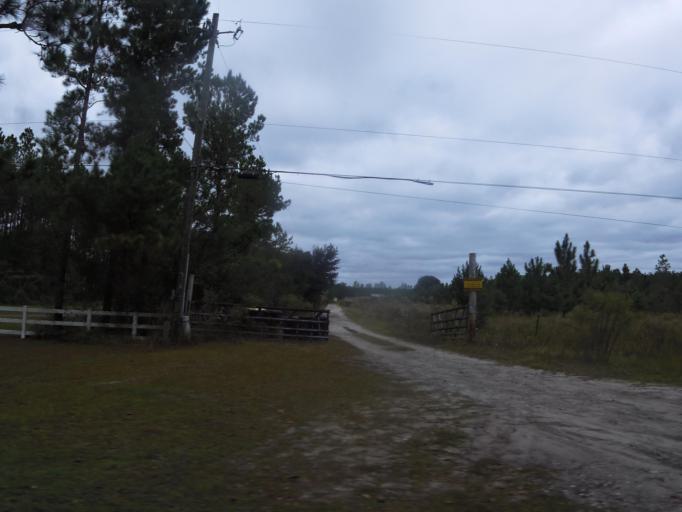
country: US
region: Florida
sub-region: Clay County
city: Lakeside
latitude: 30.2028
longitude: -81.8601
